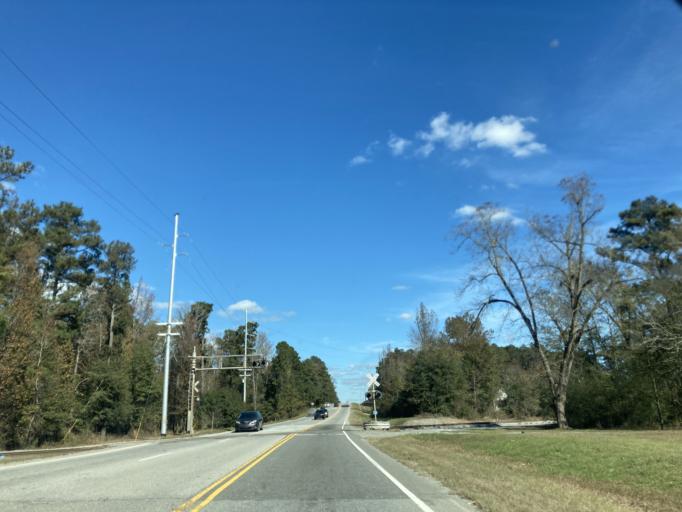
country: US
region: Georgia
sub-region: Jones County
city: Gray
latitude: 32.9204
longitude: -83.5128
